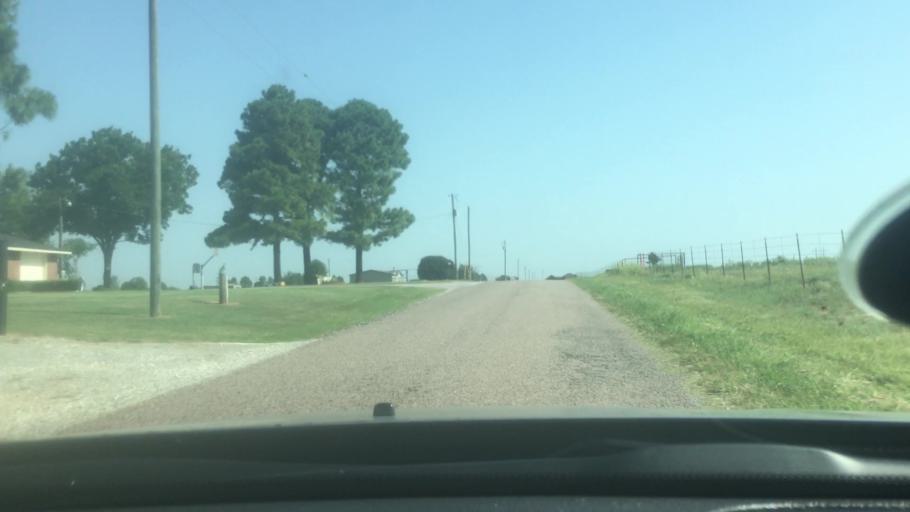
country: US
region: Oklahoma
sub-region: Bryan County
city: Calera
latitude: 33.9489
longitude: -96.4613
